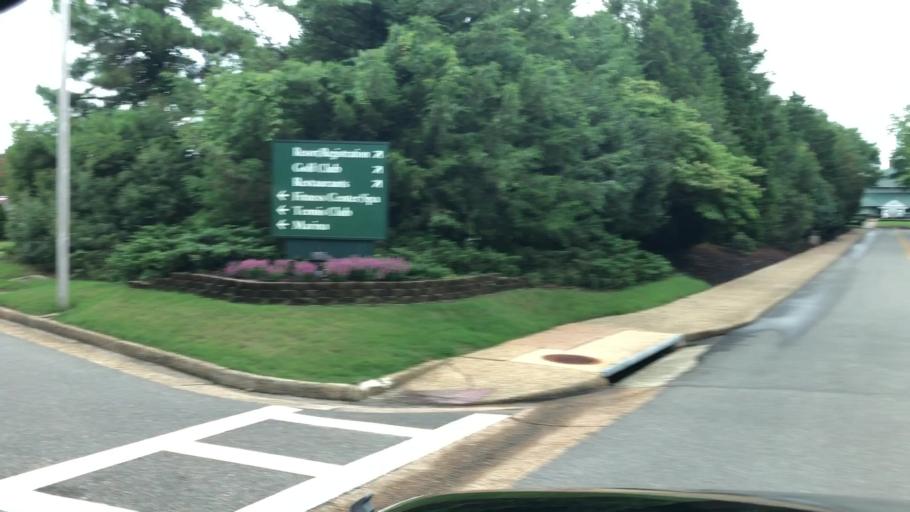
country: US
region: Virginia
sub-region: City of Williamsburg
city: Williamsburg
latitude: 37.2271
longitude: -76.6663
